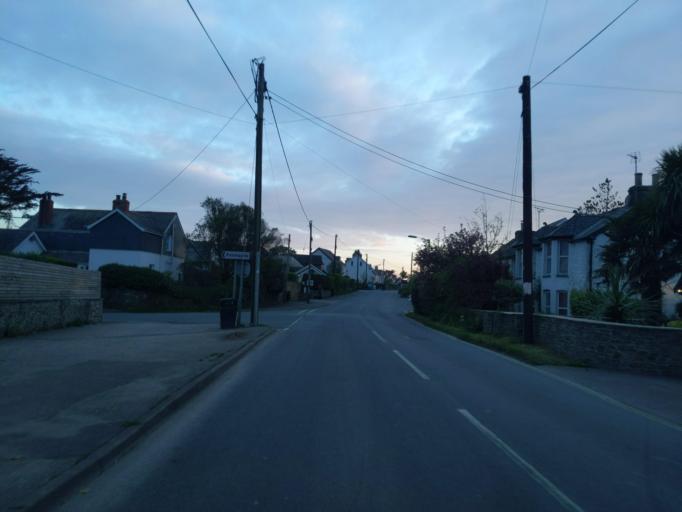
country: GB
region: England
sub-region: Cornwall
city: Polzeath
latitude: 50.5506
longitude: -4.9015
